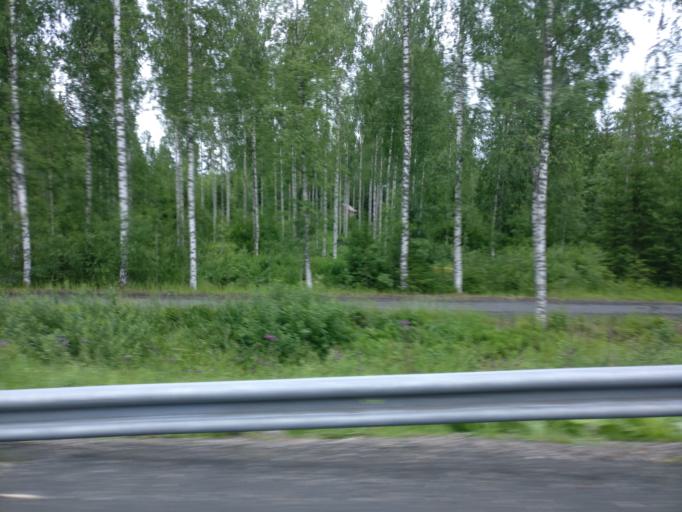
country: FI
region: Northern Savo
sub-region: Varkaus
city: Leppaevirta
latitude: 62.5985
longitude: 27.6091
